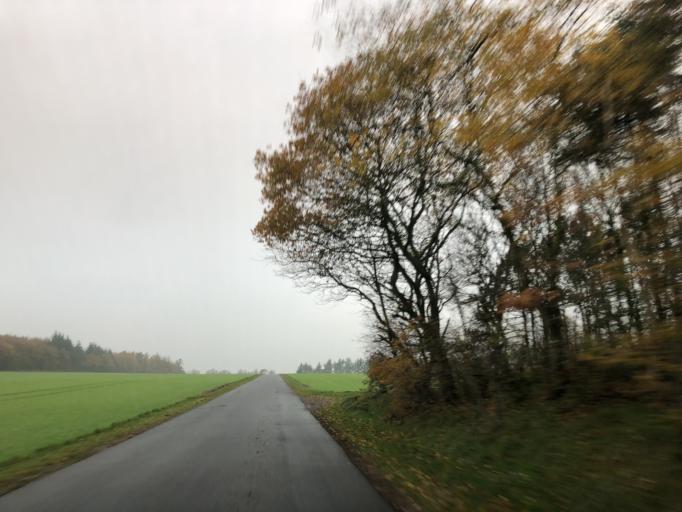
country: DK
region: Central Jutland
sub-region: Herning Kommune
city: Vildbjerg
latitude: 56.2020
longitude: 8.6814
